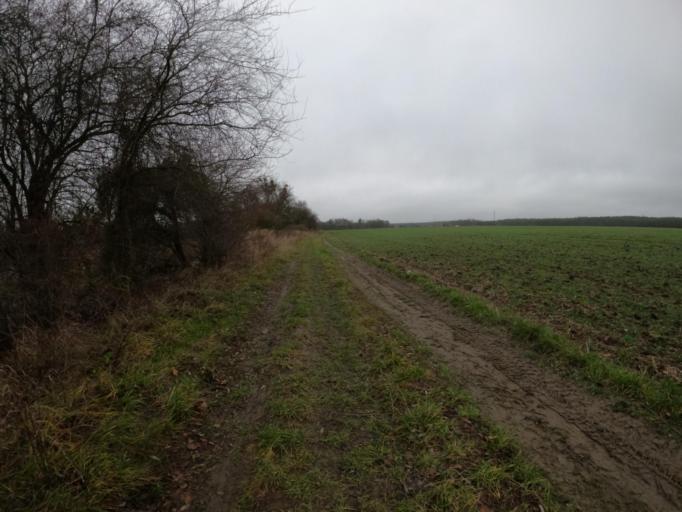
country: PL
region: West Pomeranian Voivodeship
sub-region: Powiat mysliborski
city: Debno
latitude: 52.7766
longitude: 14.7599
